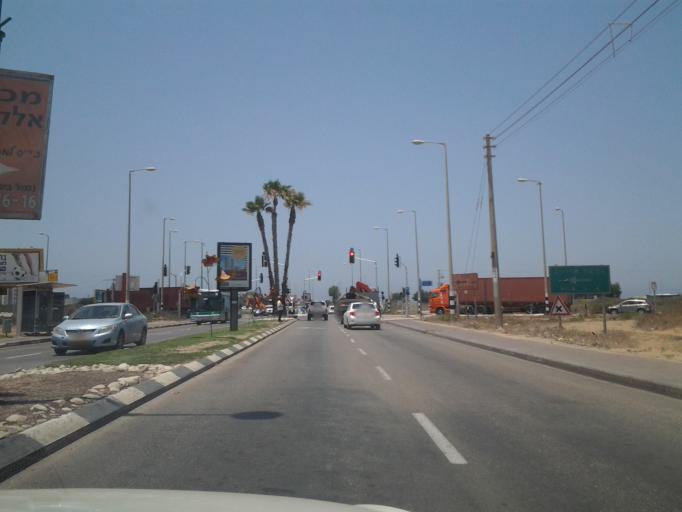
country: IL
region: Haifa
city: Hadera
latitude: 32.4463
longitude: 34.8954
